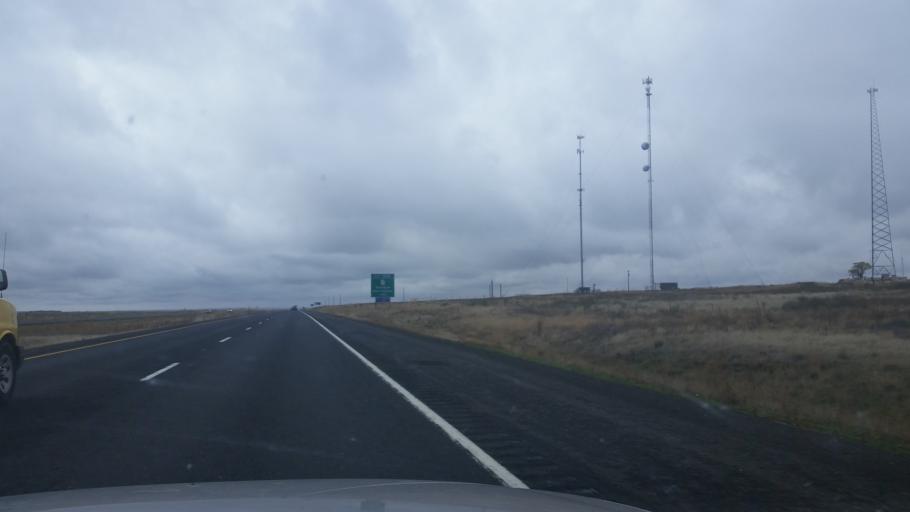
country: US
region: Washington
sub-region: Spokane County
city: Medical Lake
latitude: 47.3193
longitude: -117.9493
